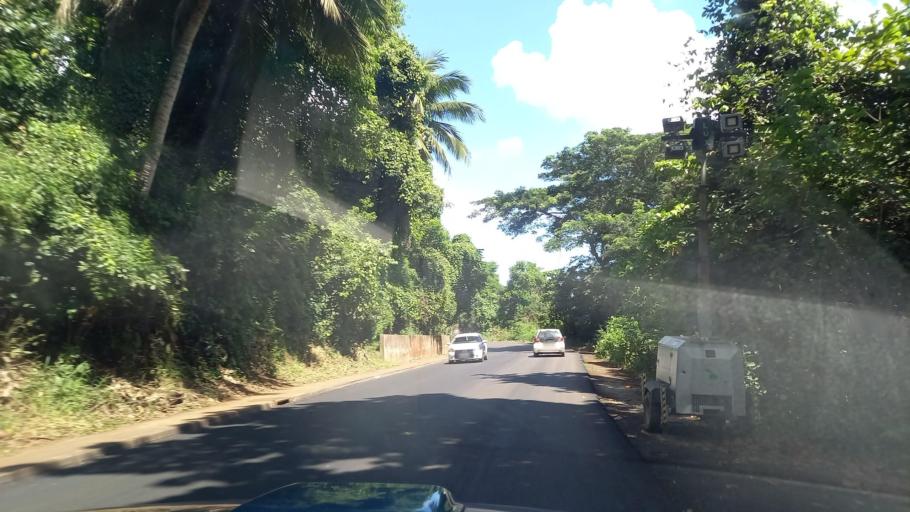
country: YT
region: Chiconi
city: Chiconi
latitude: -12.8413
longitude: 45.1195
